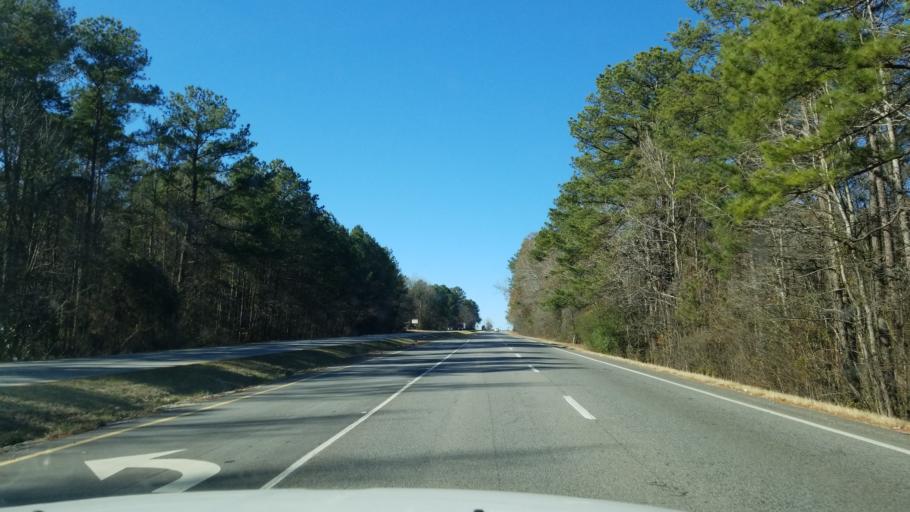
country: US
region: Alabama
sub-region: Tuscaloosa County
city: Northport
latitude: 33.2484
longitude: -87.6791
